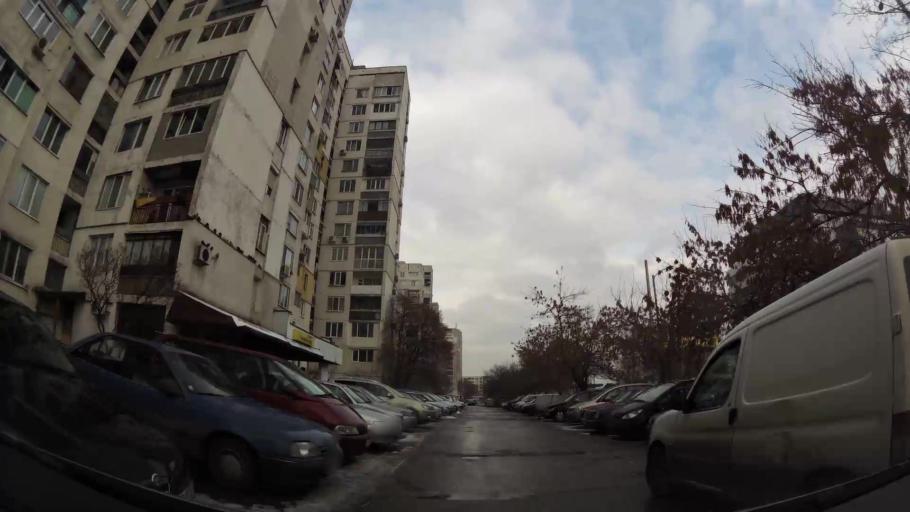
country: BG
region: Sofia-Capital
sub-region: Stolichna Obshtina
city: Sofia
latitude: 42.7132
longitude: 23.2649
